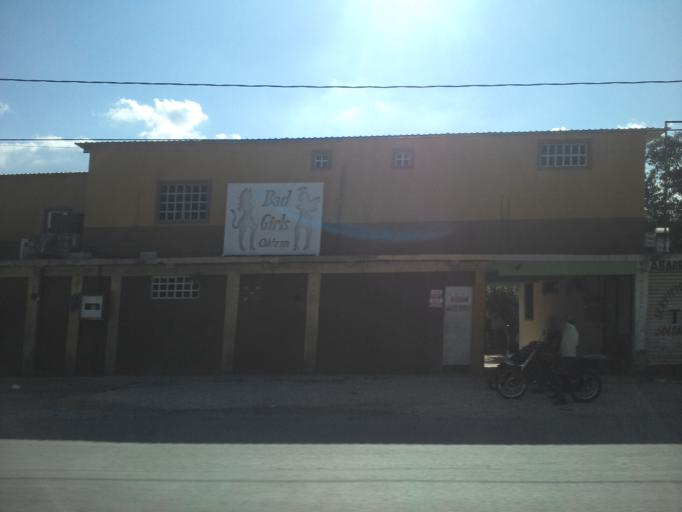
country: MX
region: Chiapas
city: Palenque
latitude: 17.5151
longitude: -91.9929
